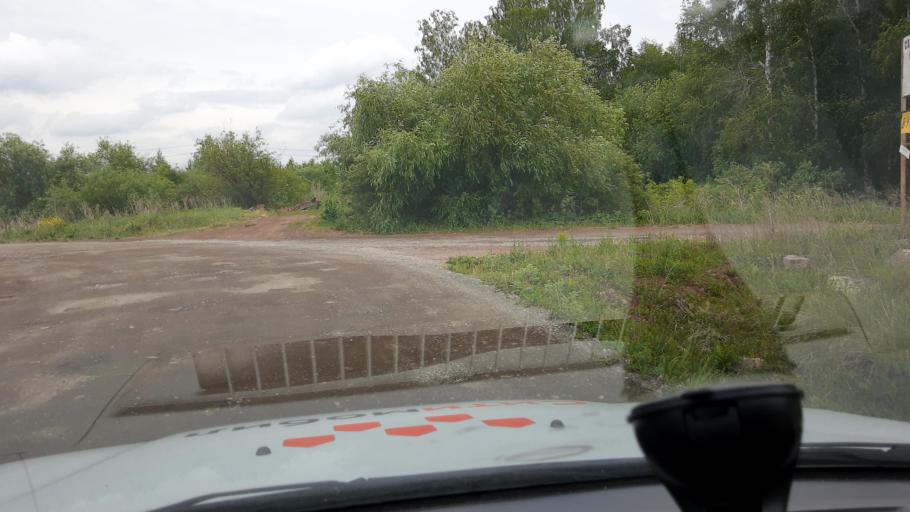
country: RU
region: Bashkortostan
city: Avdon
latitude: 54.6544
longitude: 55.6550
